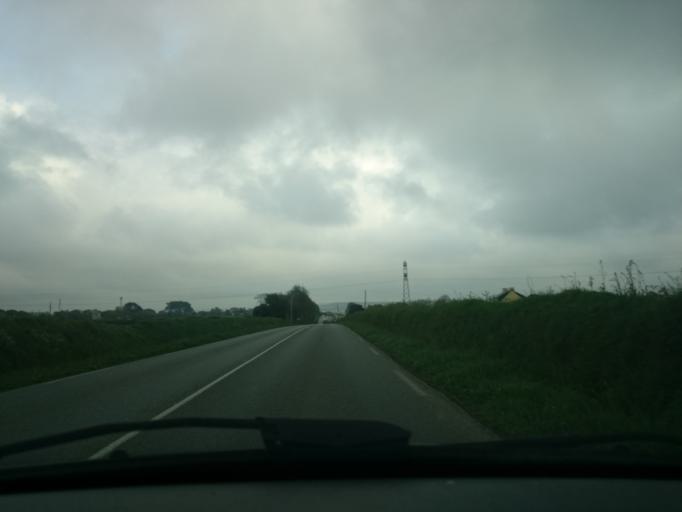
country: FR
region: Brittany
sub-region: Departement du Finistere
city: Saint-Renan
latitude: 48.4537
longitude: -4.6248
